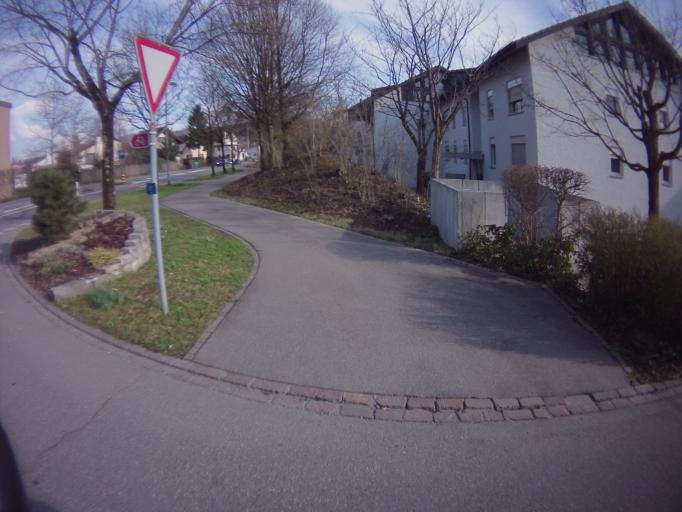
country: CH
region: Aargau
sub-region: Bezirk Baden
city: Wurenlos
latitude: 47.4467
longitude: 8.3586
